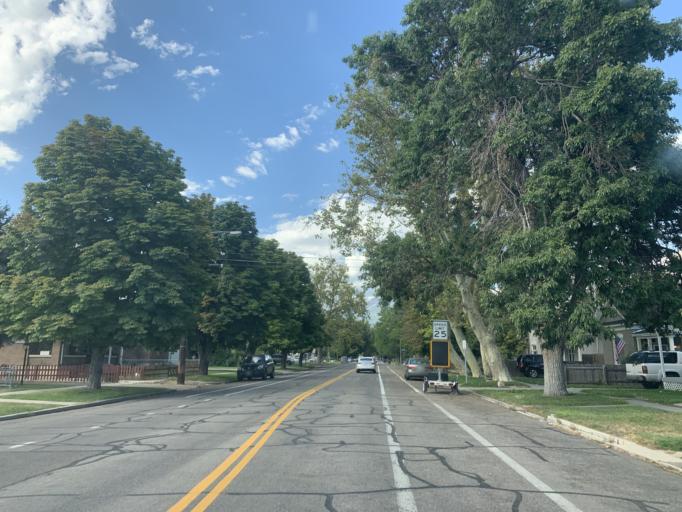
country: US
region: Utah
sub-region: Utah County
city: Provo
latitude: 40.2301
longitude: -111.6511
